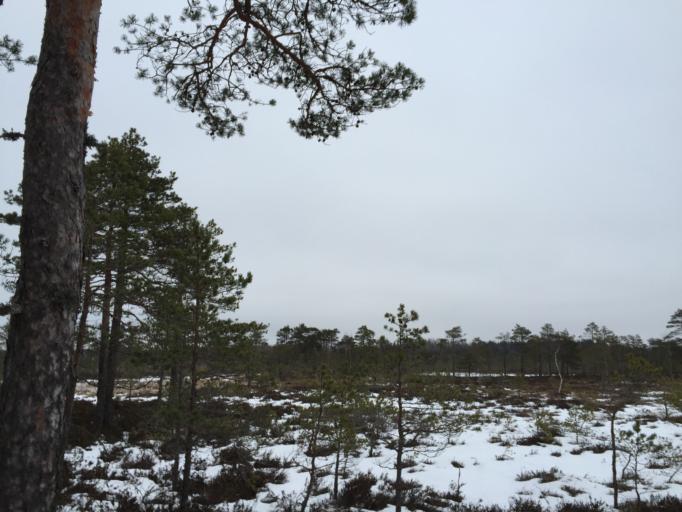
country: LV
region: Saulkrastu
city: Saulkrasti
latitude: 57.2333
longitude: 24.5051
